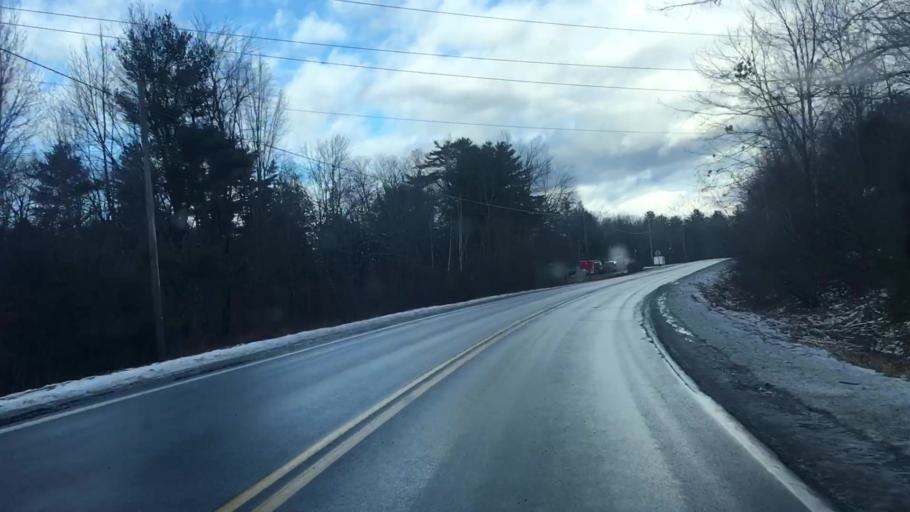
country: US
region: Maine
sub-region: Hancock County
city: Dedham
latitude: 44.6468
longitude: -68.6911
